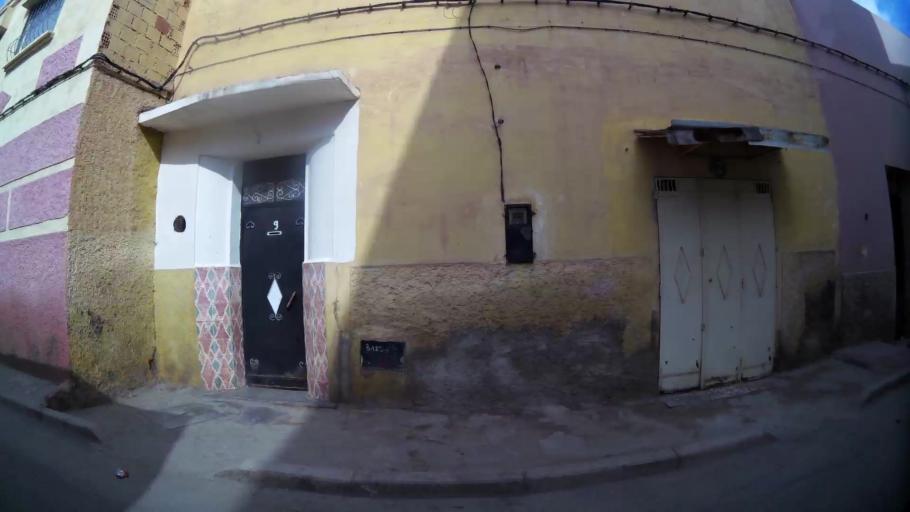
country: MA
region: Oriental
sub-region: Oujda-Angad
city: Oujda
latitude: 34.6906
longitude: -1.9040
